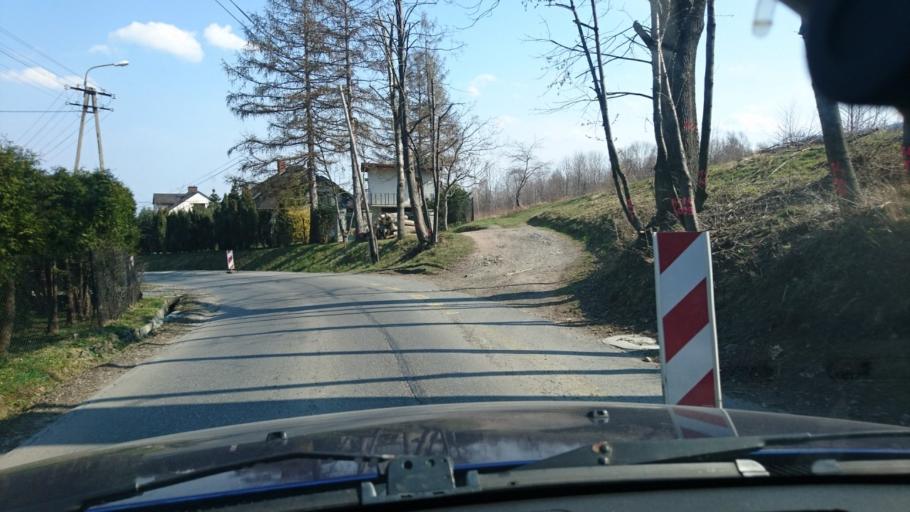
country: PL
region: Silesian Voivodeship
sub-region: Powiat bielski
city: Kozy
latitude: 49.8196
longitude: 19.1159
